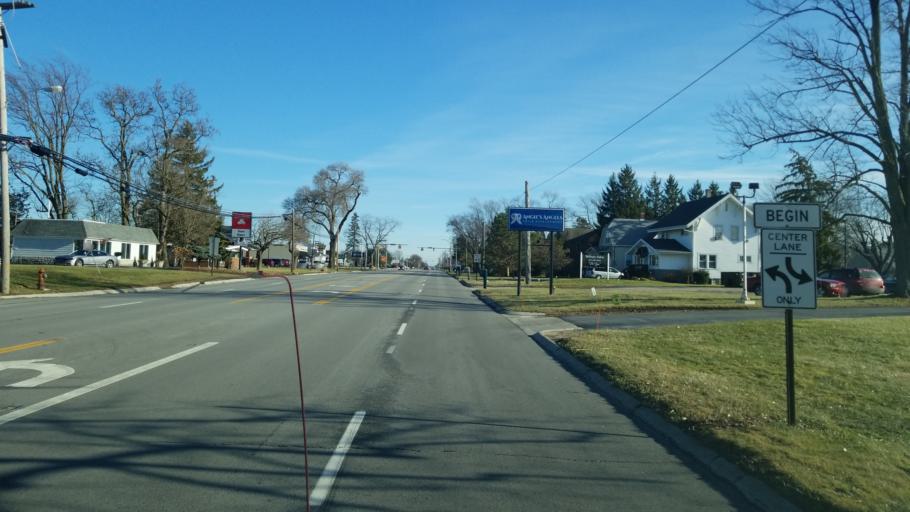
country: US
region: Ohio
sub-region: Sandusky County
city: Fremont
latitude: 41.3416
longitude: -83.0922
